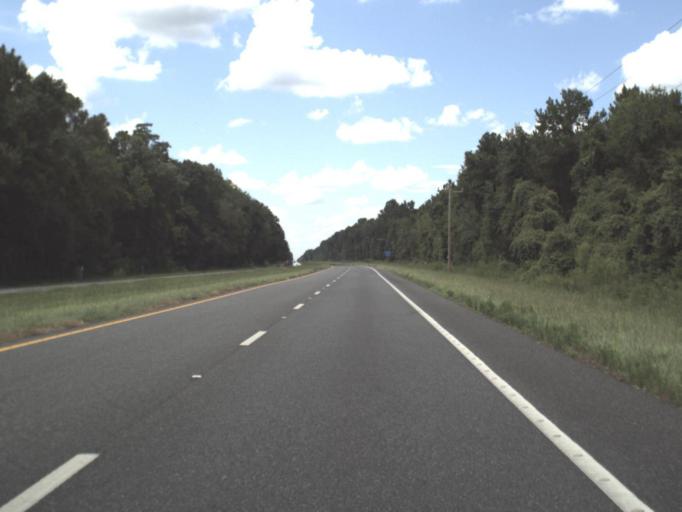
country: US
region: Florida
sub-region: Taylor County
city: Perry
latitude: 30.1871
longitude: -83.6430
